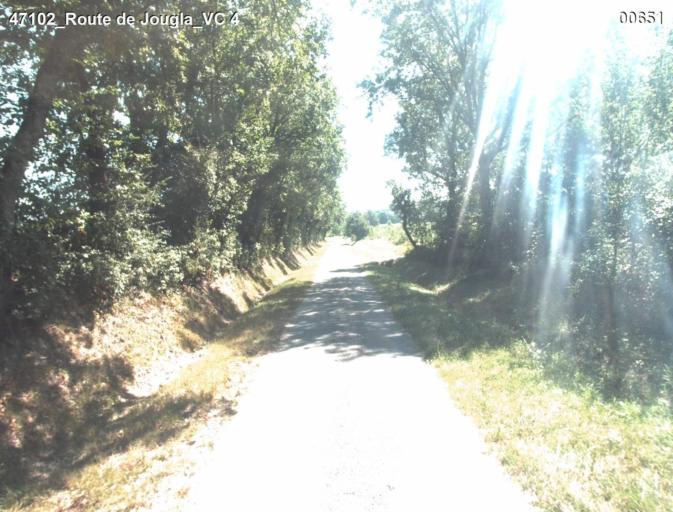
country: FR
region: Aquitaine
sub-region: Departement du Lot-et-Garonne
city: Laplume
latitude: 44.0505
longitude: 0.4437
